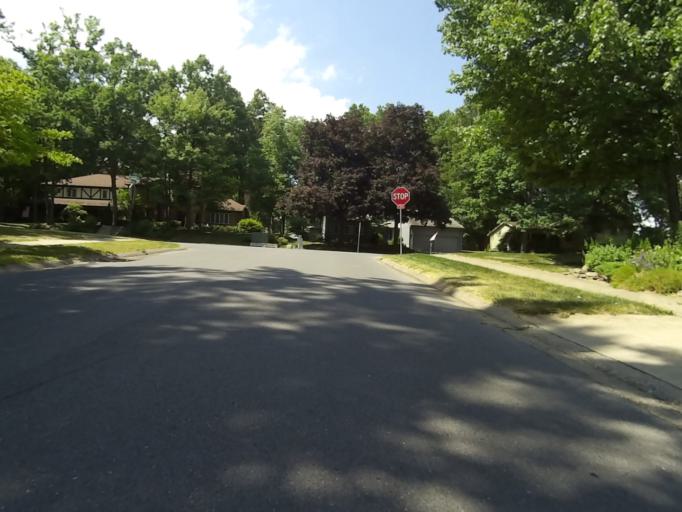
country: US
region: Pennsylvania
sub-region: Centre County
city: Park Forest Village
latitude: 40.7964
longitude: -77.9100
